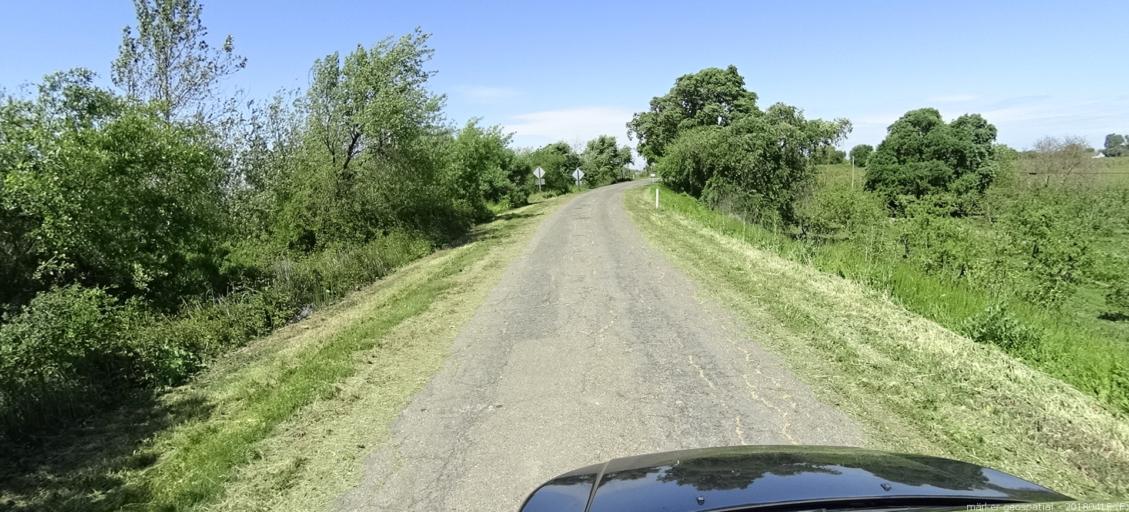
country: US
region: California
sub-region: Sacramento County
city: Walnut Grove
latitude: 38.2948
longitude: -121.6046
